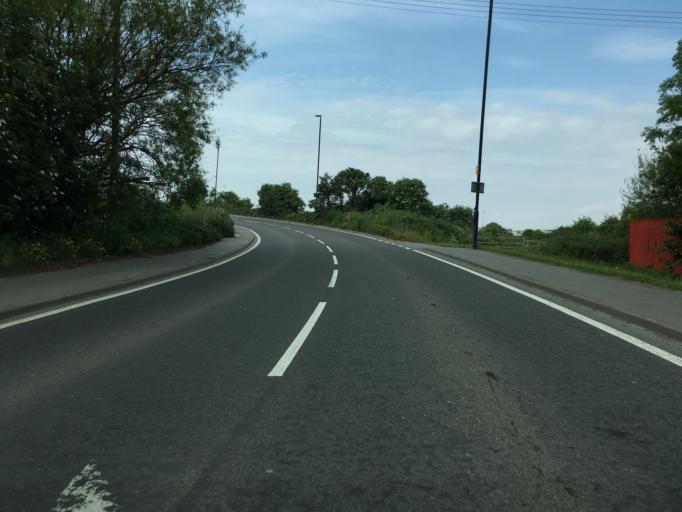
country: GB
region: England
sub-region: South Gloucestershire
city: Severn Beach
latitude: 51.5278
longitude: -2.6823
